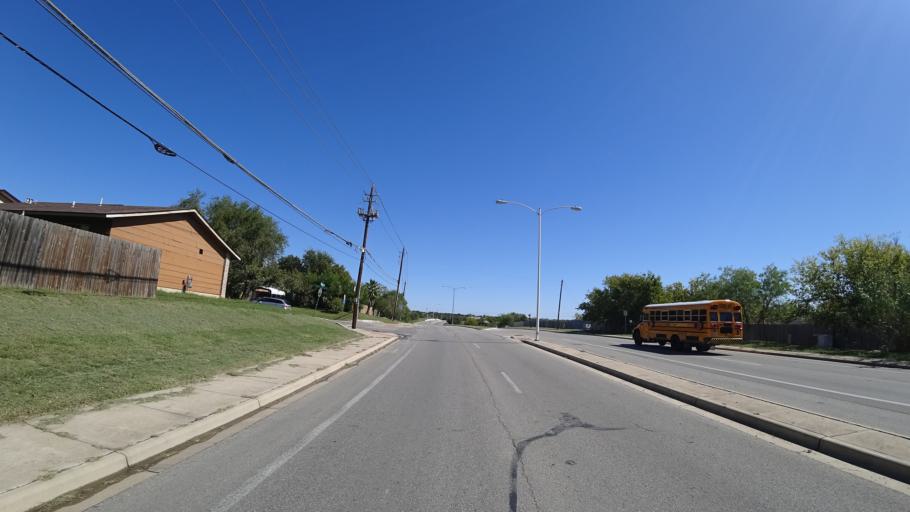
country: US
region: Texas
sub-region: Travis County
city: Hornsby Bend
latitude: 30.2984
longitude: -97.6441
